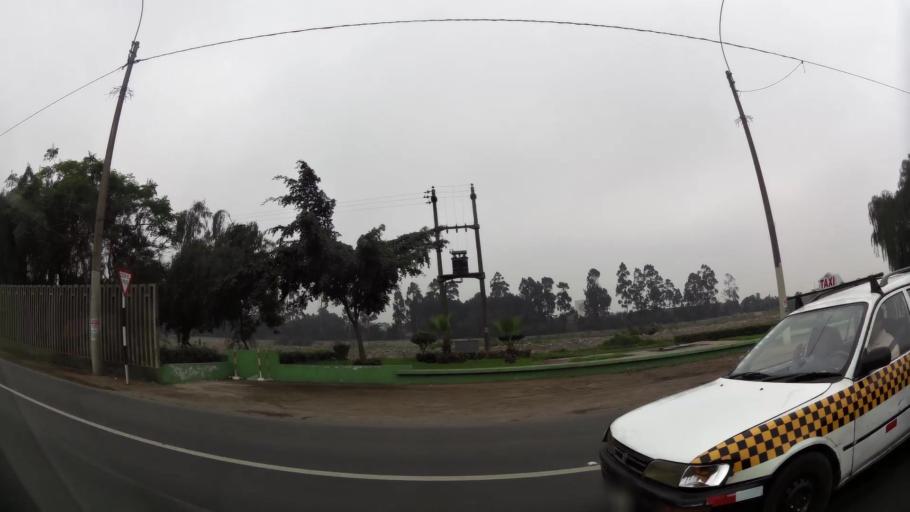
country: PE
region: Lima
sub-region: Lima
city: Vitarte
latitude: -12.0207
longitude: -76.9536
